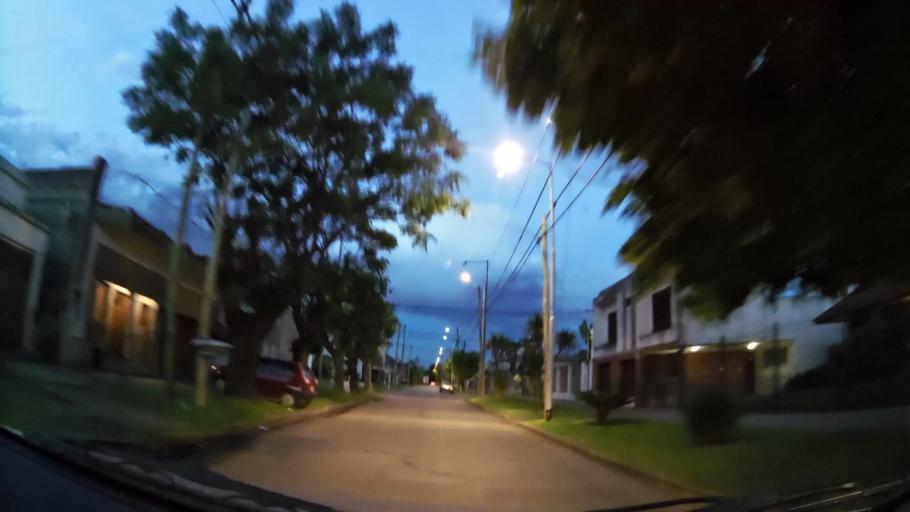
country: AR
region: Buenos Aires
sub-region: Partido de Quilmes
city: Quilmes
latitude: -34.6962
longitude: -58.3106
